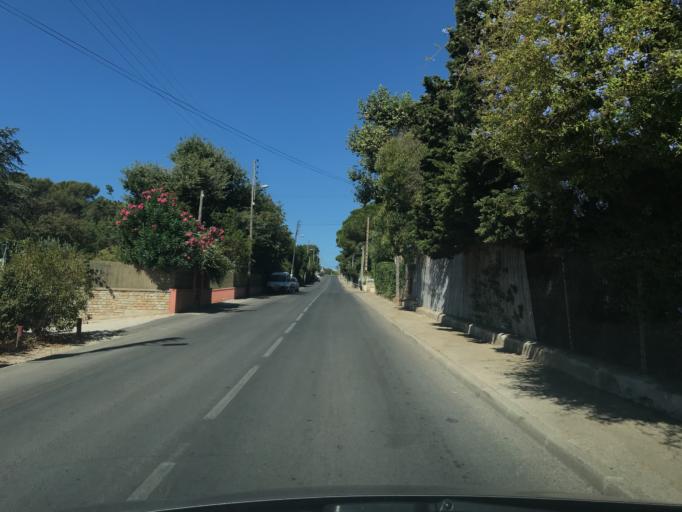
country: FR
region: Provence-Alpes-Cote d'Azur
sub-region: Departement du Var
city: La Seyne-sur-Mer
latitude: 43.0983
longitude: 5.9068
